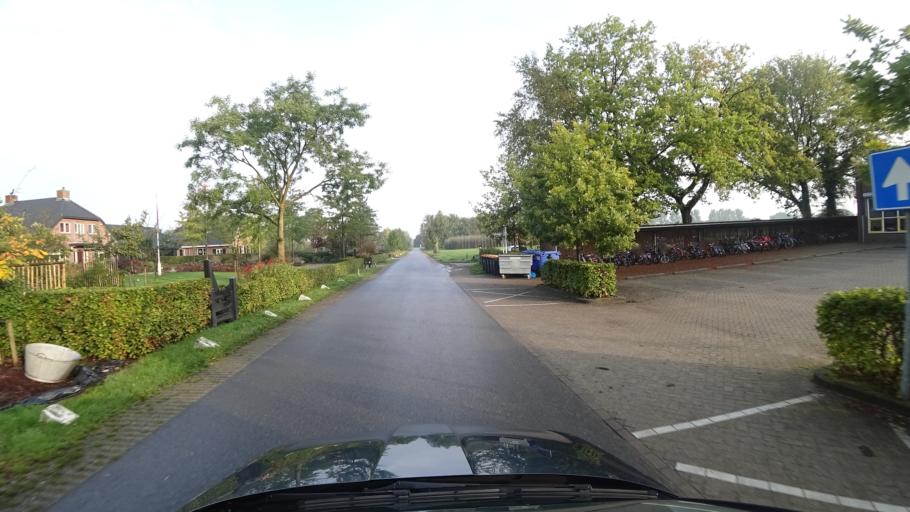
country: NL
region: Gelderland
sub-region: Gemeente Ede
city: Ede
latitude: 52.0120
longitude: 5.6256
